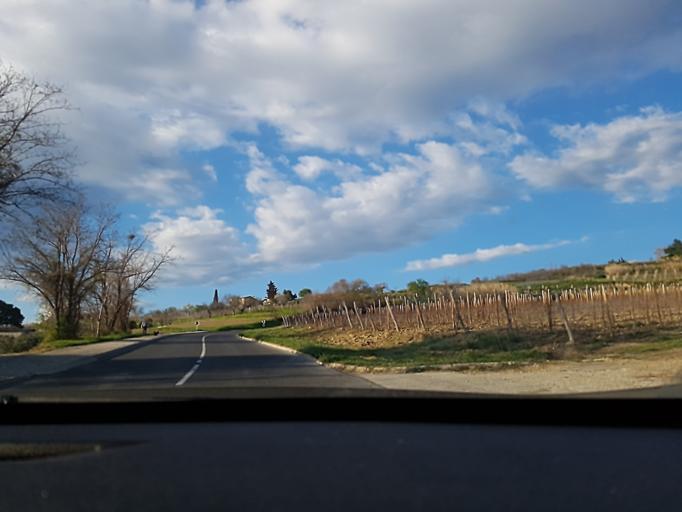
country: SI
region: Izola-Isola
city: Izola
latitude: 45.5415
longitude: 13.6817
